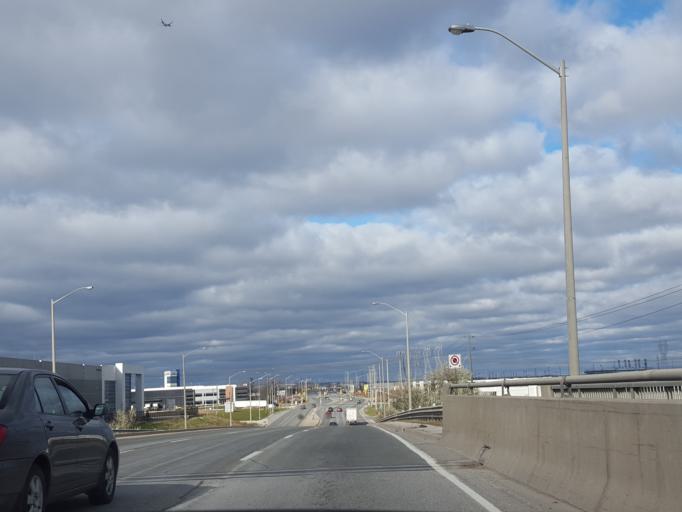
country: CA
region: Ontario
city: Brampton
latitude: 43.7177
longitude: -79.6610
